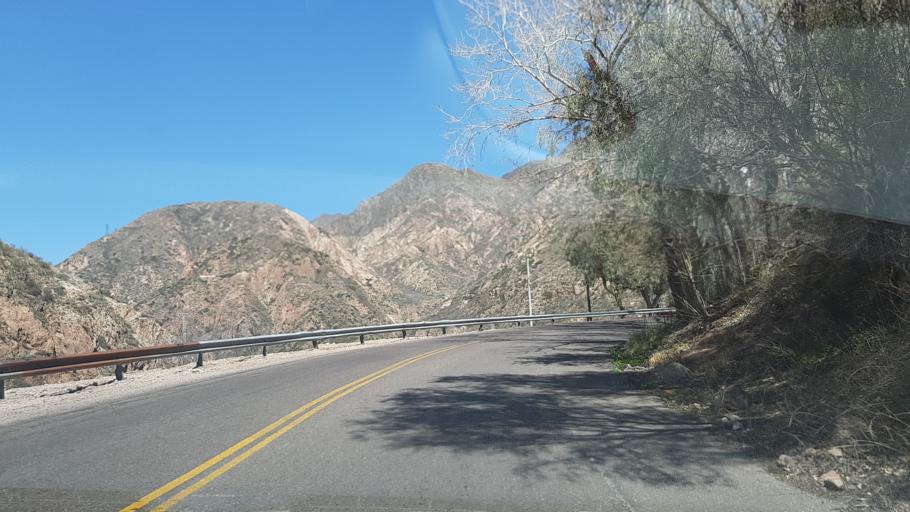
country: AR
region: Mendoza
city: Lujan de Cuyo
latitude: -33.0239
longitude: -69.1143
